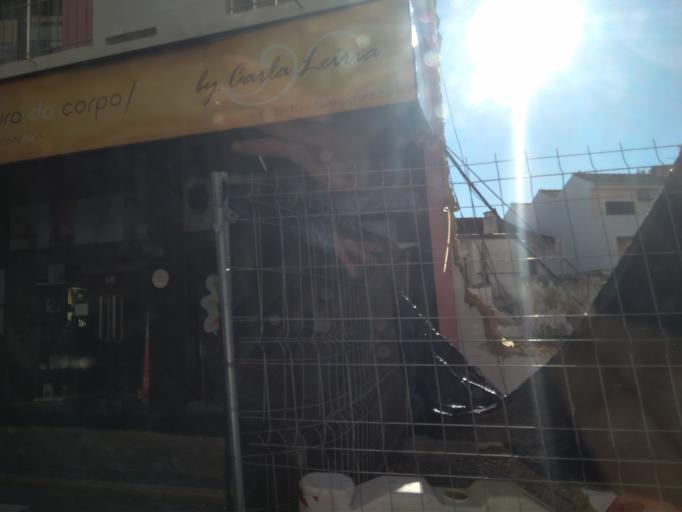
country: PT
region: Faro
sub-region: Faro
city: Faro
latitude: 37.0189
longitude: -7.9379
